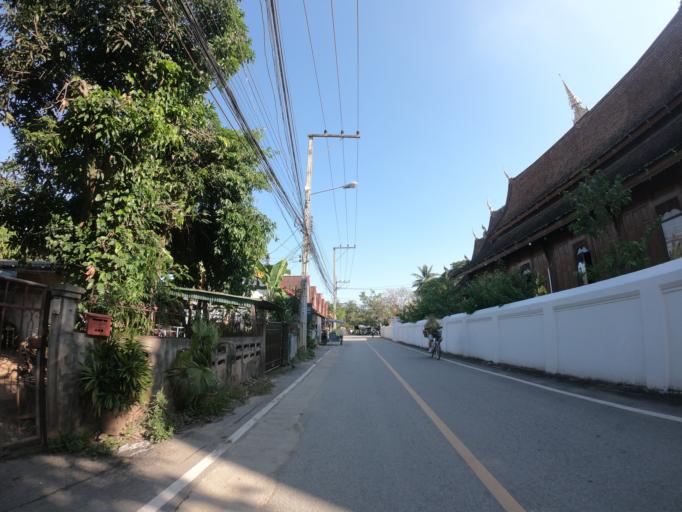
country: TH
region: Chiang Mai
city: San Sai
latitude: 18.8318
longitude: 99.0343
